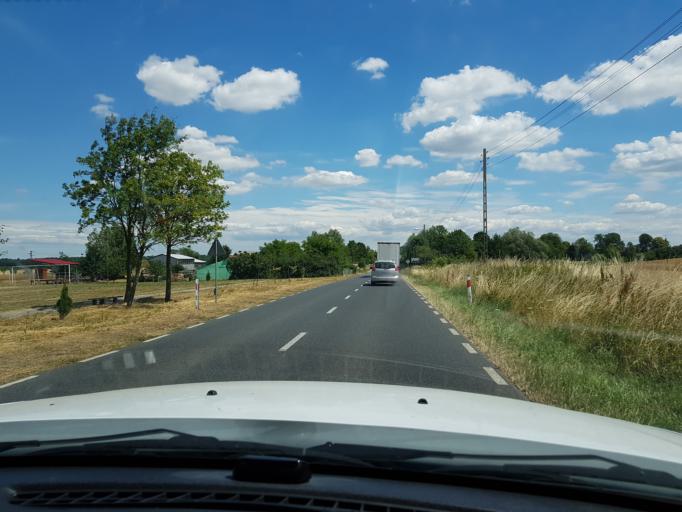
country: PL
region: West Pomeranian Voivodeship
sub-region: Powiat mysliborski
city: Nowogrodek Pomorski
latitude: 52.9071
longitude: 14.9481
